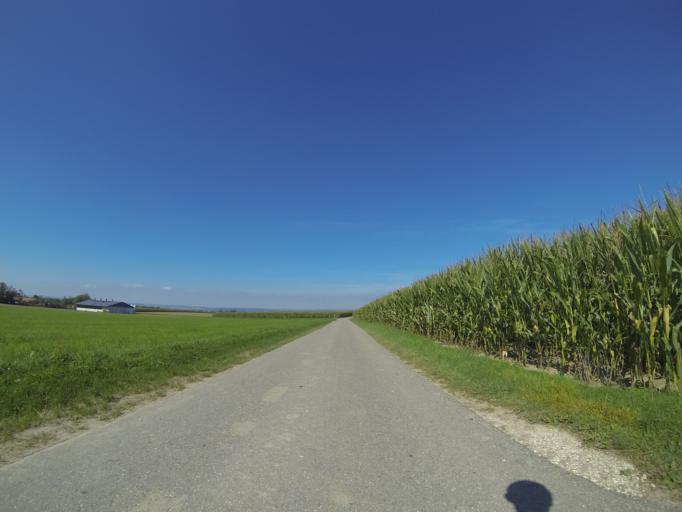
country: DE
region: Baden-Wuerttemberg
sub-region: Tuebingen Region
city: Achstetten
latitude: 48.2636
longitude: 9.9219
